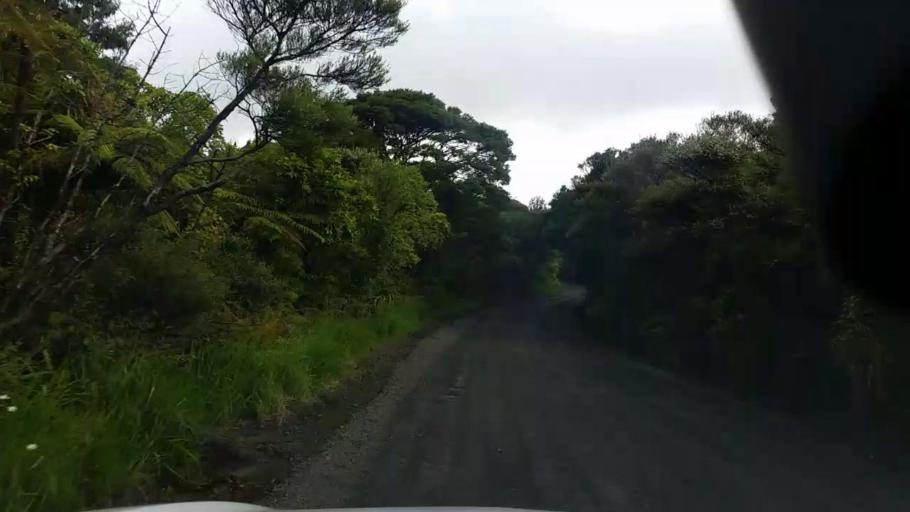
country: NZ
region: Auckland
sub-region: Auckland
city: Titirangi
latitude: -36.9448
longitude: 174.5262
